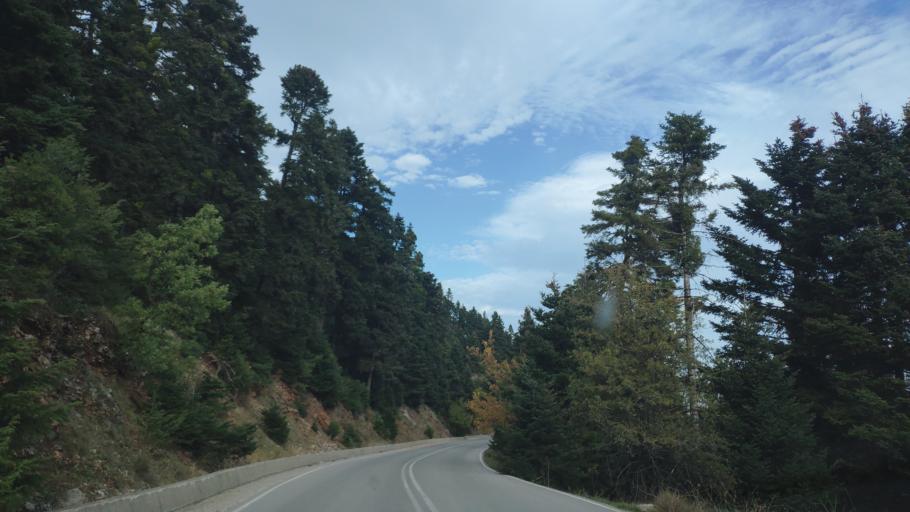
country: GR
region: Central Greece
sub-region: Nomos Fokidos
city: Amfissa
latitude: 38.6589
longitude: 22.3816
